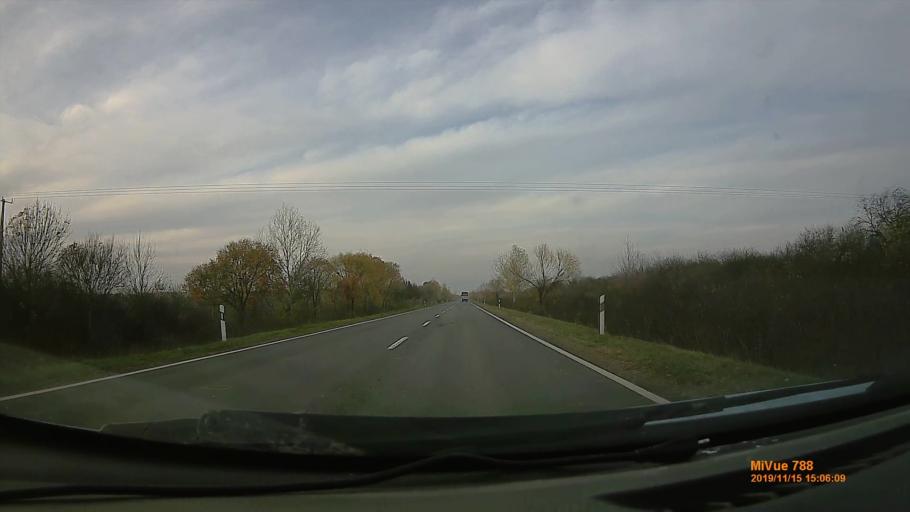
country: HU
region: Bekes
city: Gyula
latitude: 46.6397
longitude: 21.2474
